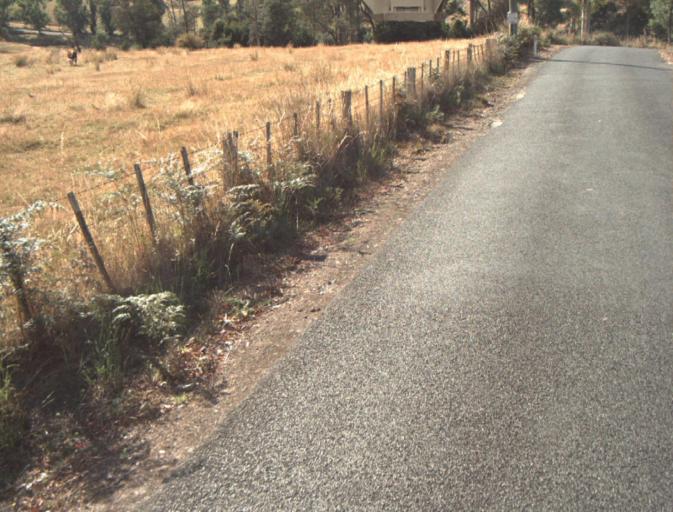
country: AU
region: Tasmania
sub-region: Launceston
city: Mayfield
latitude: -41.2871
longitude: 147.2065
